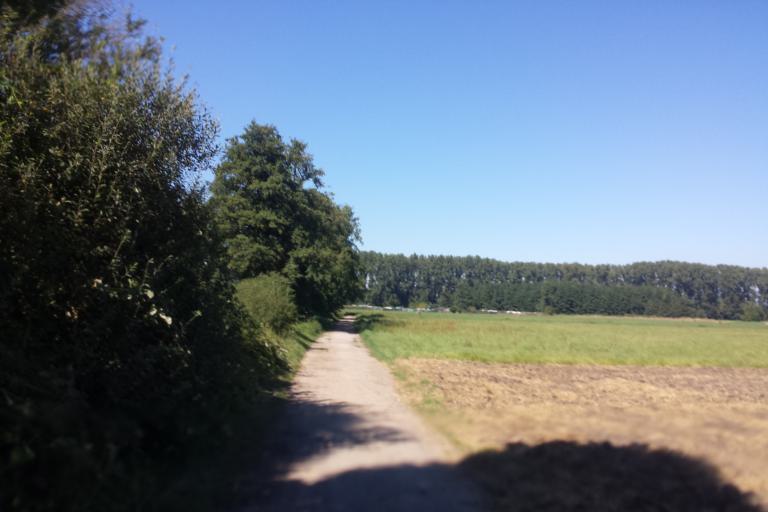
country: DE
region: Hesse
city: Viernheim
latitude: 49.5881
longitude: 8.5963
